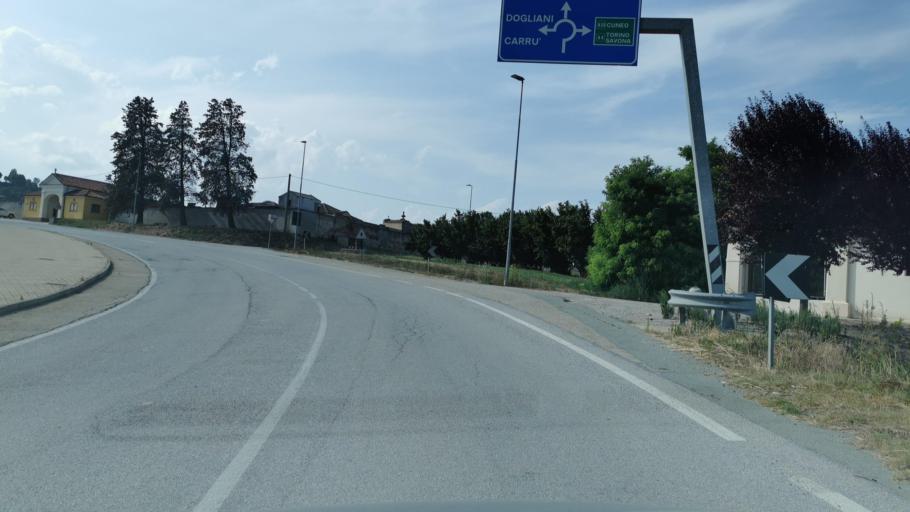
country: IT
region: Piedmont
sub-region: Provincia di Cuneo
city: Cherasco
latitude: 44.6507
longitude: 7.8733
